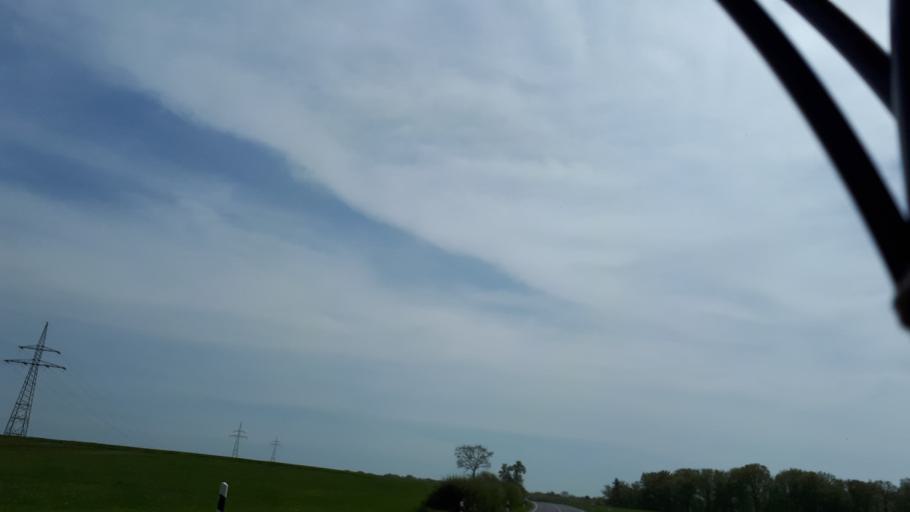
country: LU
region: Luxembourg
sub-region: Canton de Luxembourg
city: Bertrange
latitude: 49.5965
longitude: 6.0571
